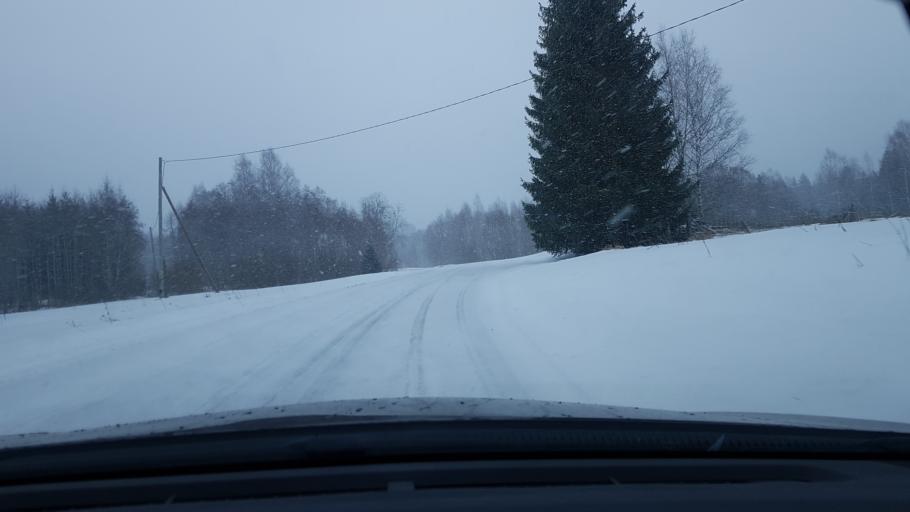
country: EE
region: Harju
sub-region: Anija vald
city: Kehra
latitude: 59.1702
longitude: 25.3624
